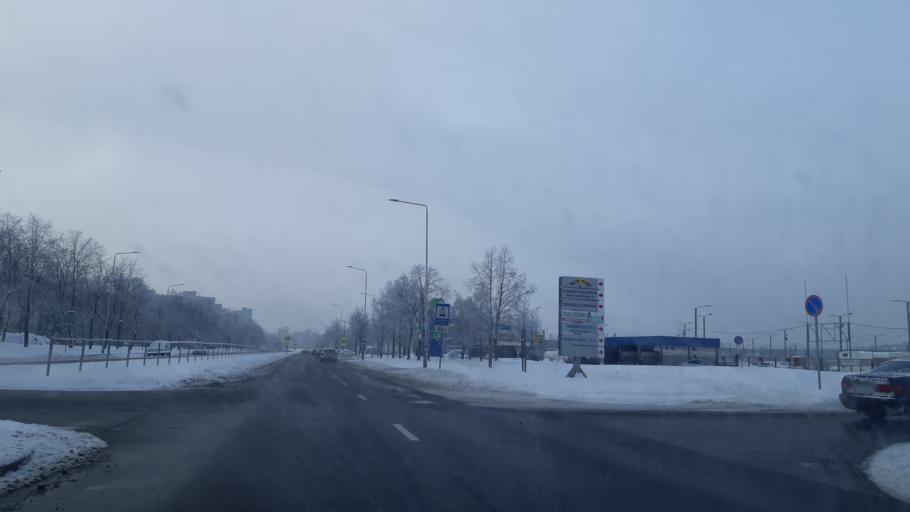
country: LT
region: Kauno apskritis
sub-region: Kaunas
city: Eiguliai
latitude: 54.9312
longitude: 23.9529
